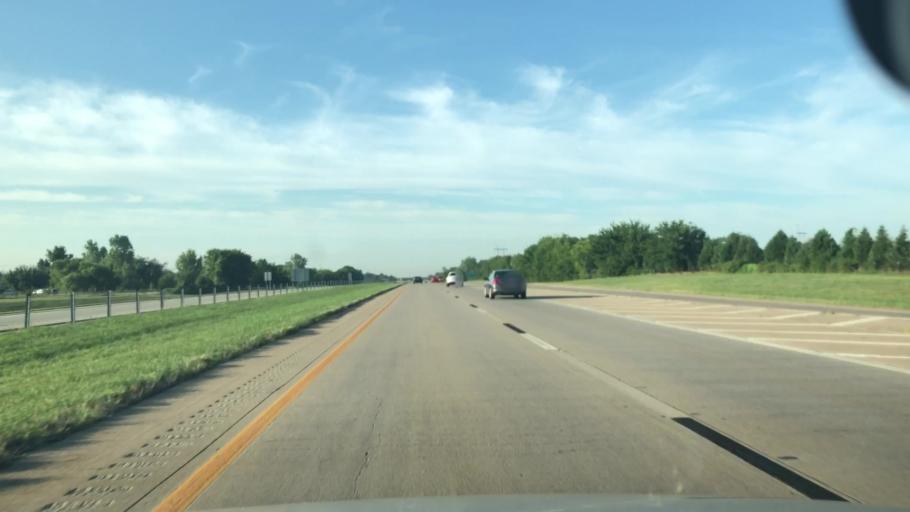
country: US
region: Oklahoma
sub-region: Tulsa County
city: Turley
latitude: 36.2763
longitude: -95.9239
